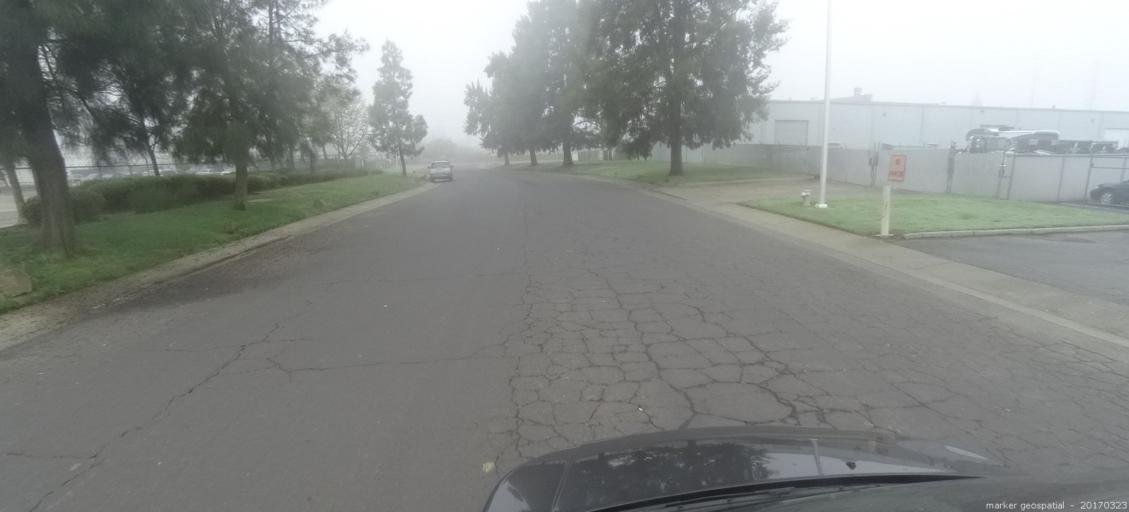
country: US
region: California
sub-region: Sacramento County
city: Florin
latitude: 38.5135
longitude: -121.4072
